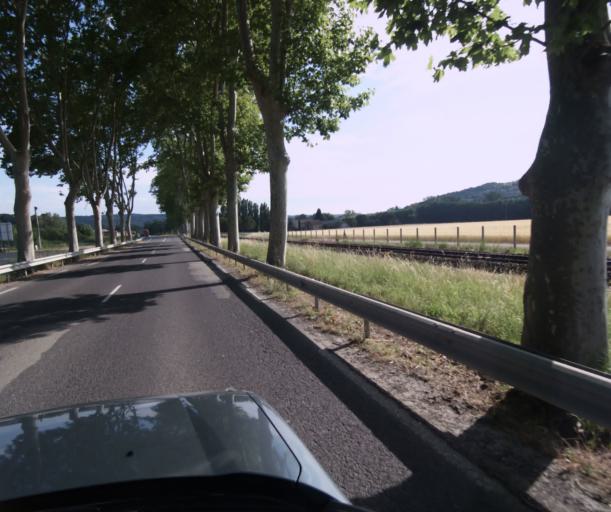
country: FR
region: Languedoc-Roussillon
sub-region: Departement de l'Aude
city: Limoux
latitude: 43.0830
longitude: 2.2251
